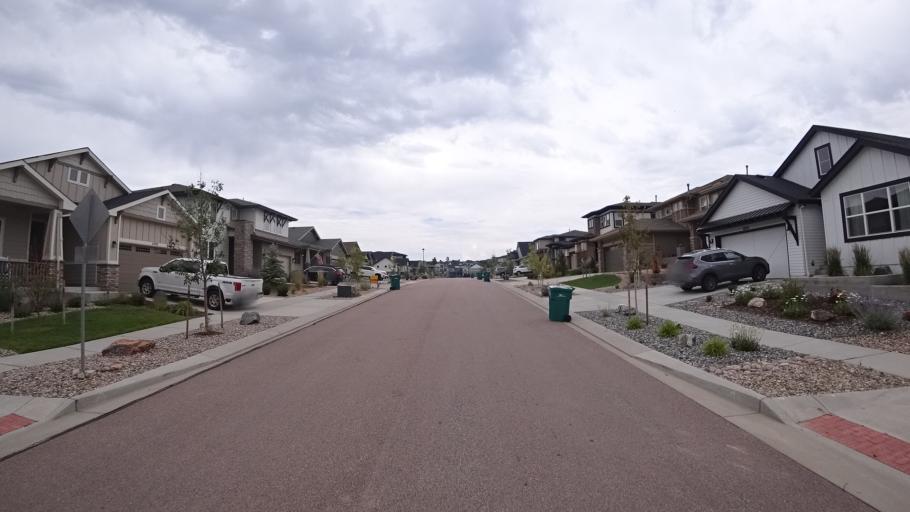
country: US
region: Colorado
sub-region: El Paso County
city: Gleneagle
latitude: 39.0016
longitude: -104.8033
